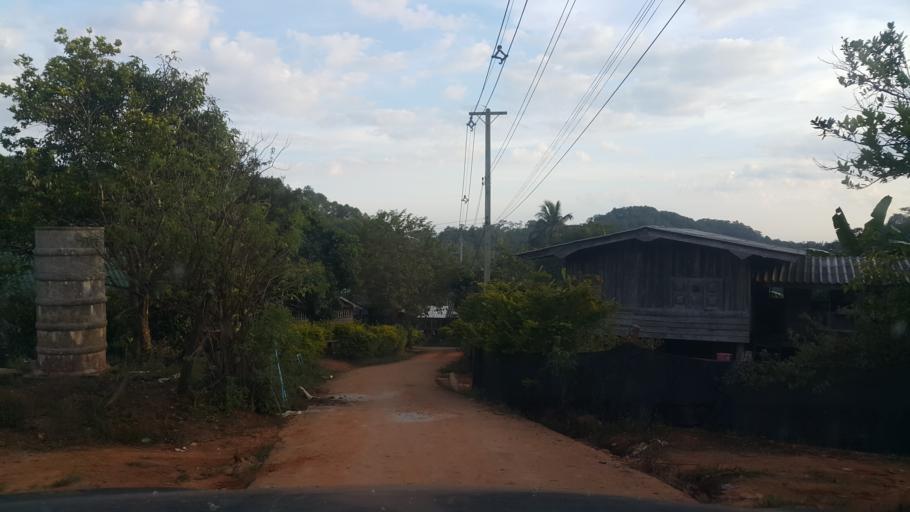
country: TH
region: Chiang Mai
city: Samoeng
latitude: 19.0074
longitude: 98.6462
